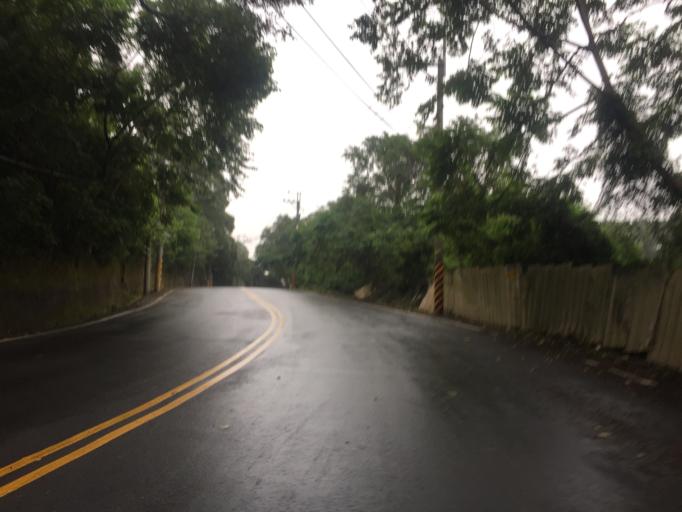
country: TW
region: Taiwan
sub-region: Hsinchu
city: Hsinchu
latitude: 24.7646
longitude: 120.9503
